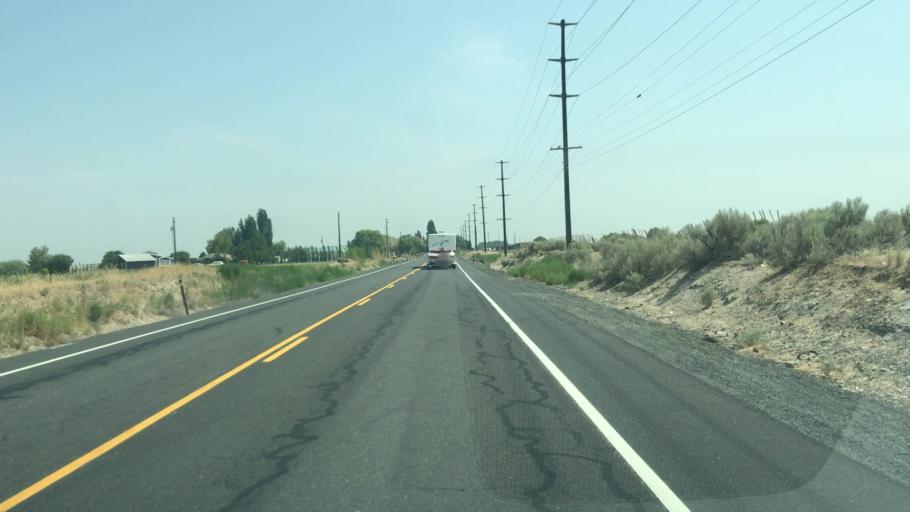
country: US
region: Washington
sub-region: Grant County
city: Quincy
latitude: 47.1603
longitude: -119.8846
